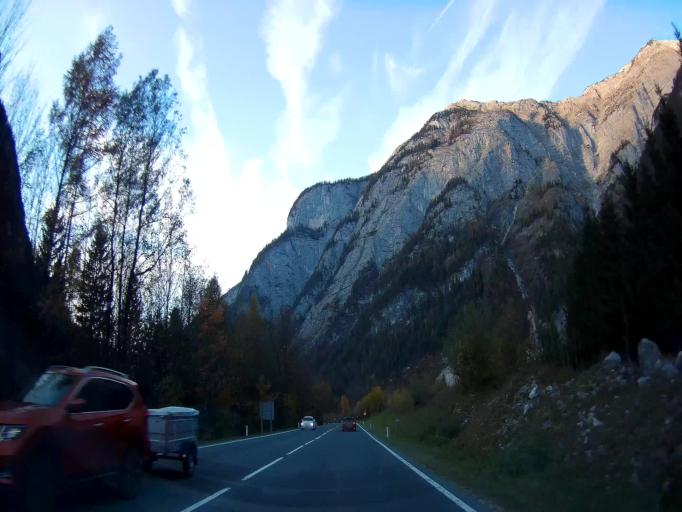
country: AT
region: Salzburg
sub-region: Politischer Bezirk Zell am See
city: Saalfelden am Steinernen Meer
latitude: 47.4849
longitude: 12.8269
